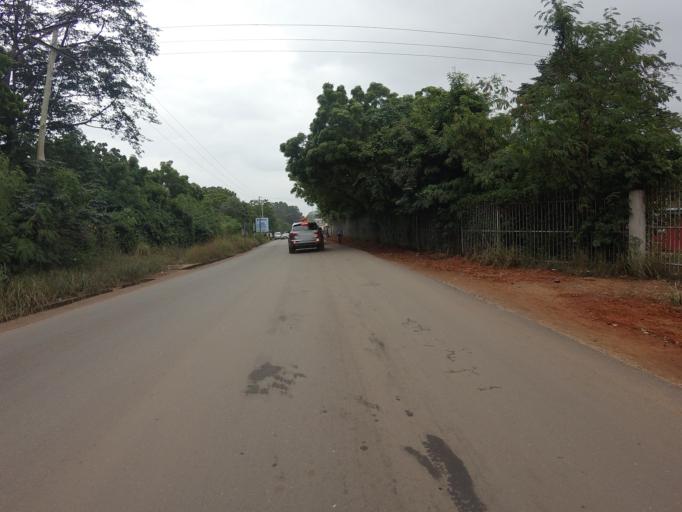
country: GH
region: Greater Accra
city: Dome
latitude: 5.6316
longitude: -0.2184
